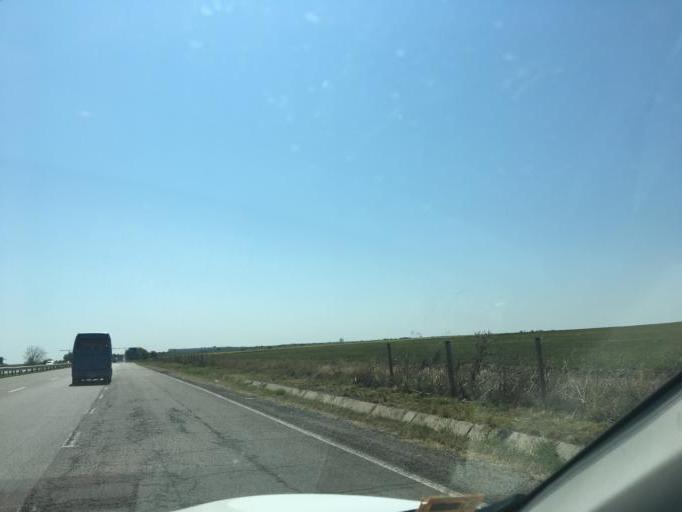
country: BG
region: Burgas
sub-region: Obshtina Kameno
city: Kameno
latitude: 42.5886
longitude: 27.3987
